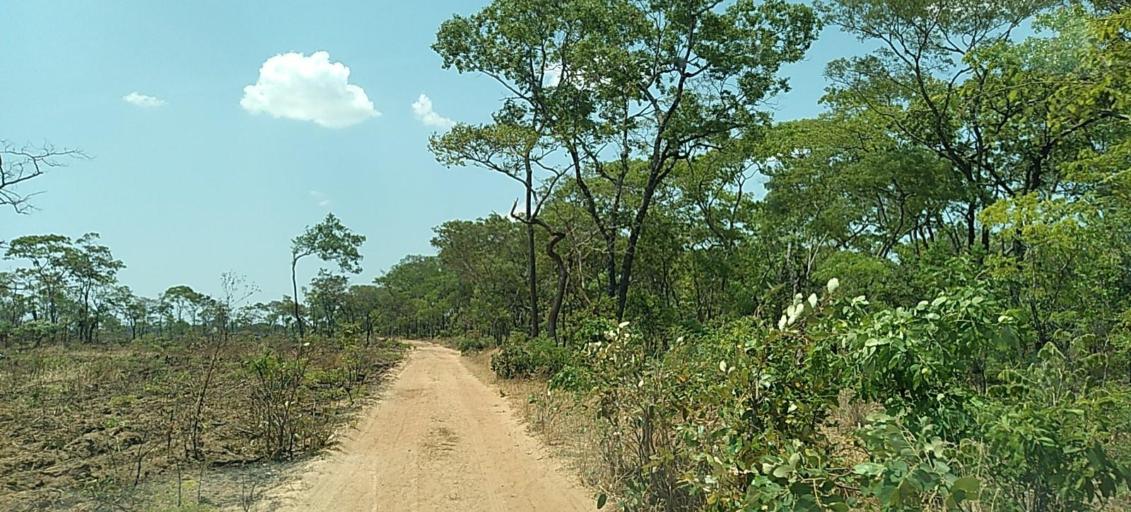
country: ZM
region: Copperbelt
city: Mpongwe
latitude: -13.6553
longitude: 28.4887
